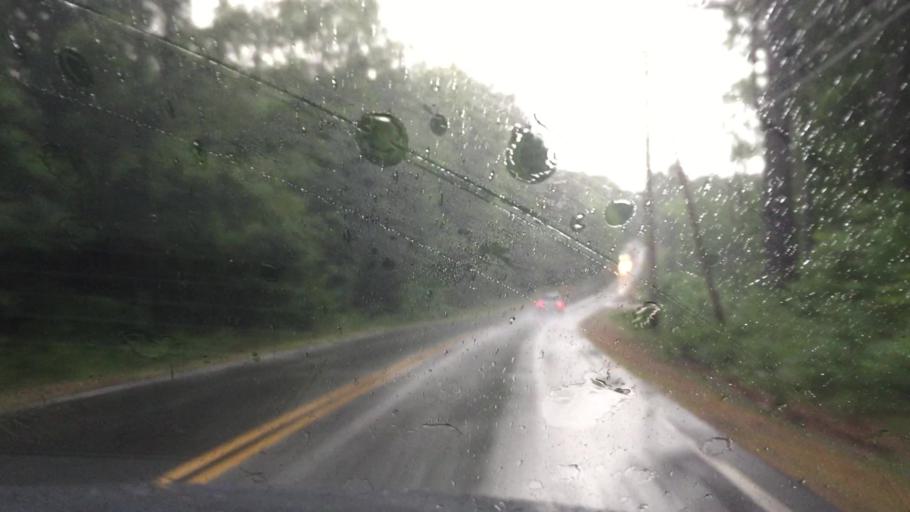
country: US
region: New Hampshire
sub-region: Grafton County
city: Holderness
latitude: 43.7205
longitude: -71.5418
